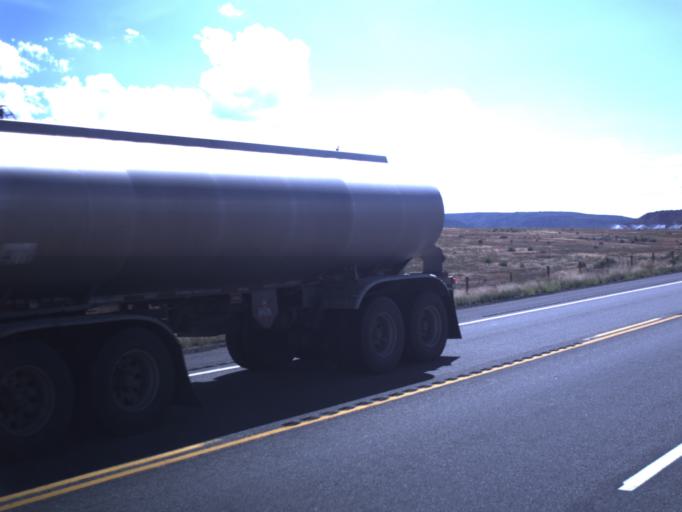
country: US
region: Utah
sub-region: Duchesne County
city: Duchesne
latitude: 40.2125
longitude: -110.8477
